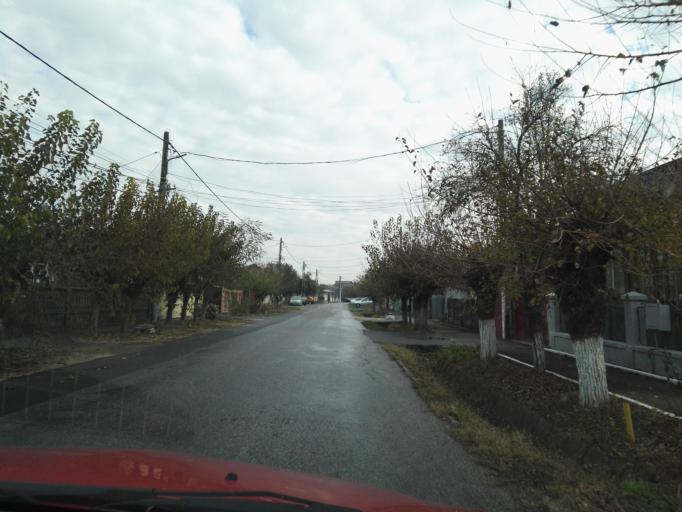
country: RO
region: Ilfov
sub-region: Comuna Jilava
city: Jilava
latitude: 44.3413
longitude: 26.0752
